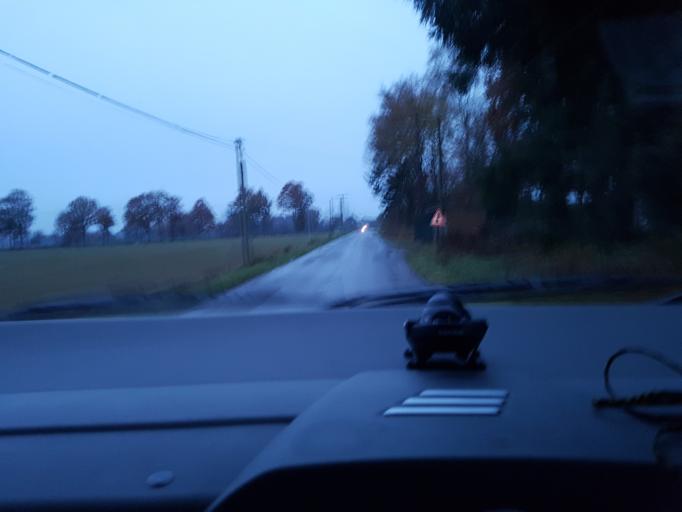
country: FR
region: Brittany
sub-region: Departement d'Ille-et-Vilaine
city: Montreuil-sous-Perouse
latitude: 48.1968
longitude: -1.2707
